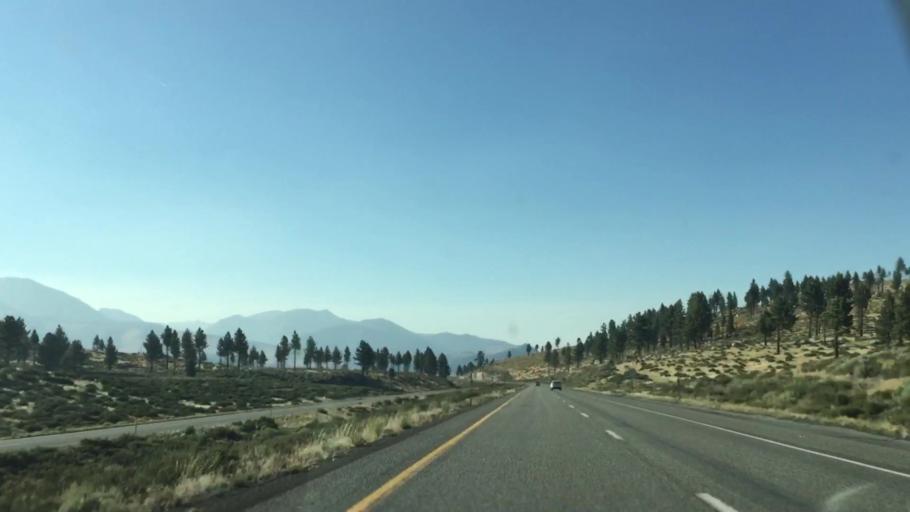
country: US
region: California
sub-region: Mono County
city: Mammoth Lakes
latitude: 37.8217
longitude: -119.0617
